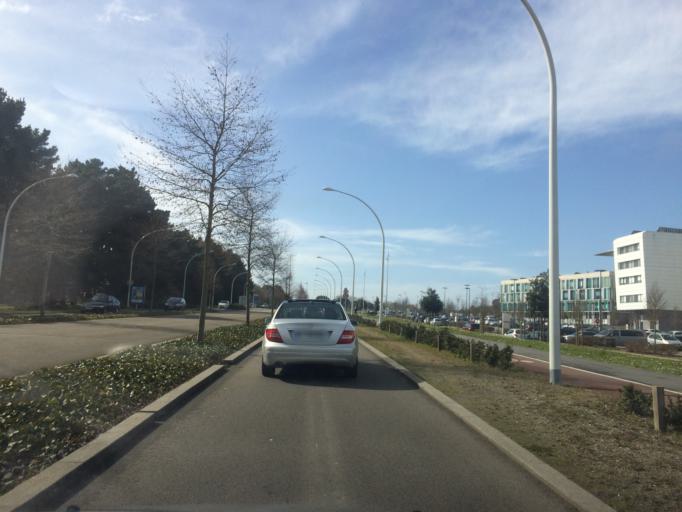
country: FR
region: Pays de la Loire
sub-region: Departement de la Loire-Atlantique
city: Saint-Nazaire
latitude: 47.2671
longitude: -2.2545
